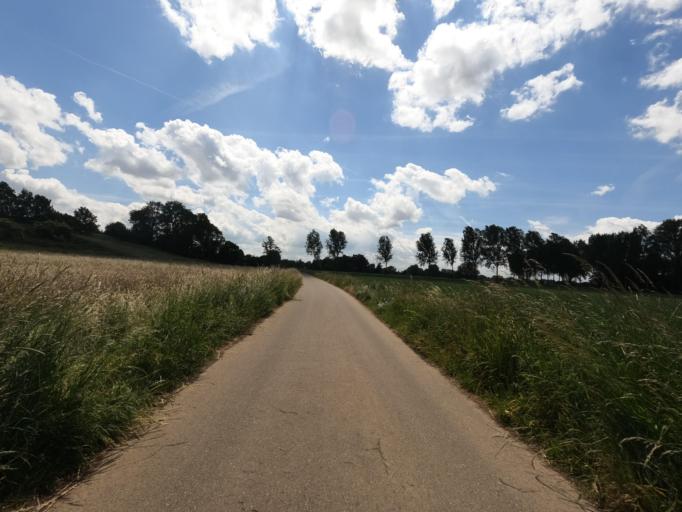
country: DE
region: North Rhine-Westphalia
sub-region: Regierungsbezirk Koln
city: Wassenberg
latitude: 51.0782
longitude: 6.1590
